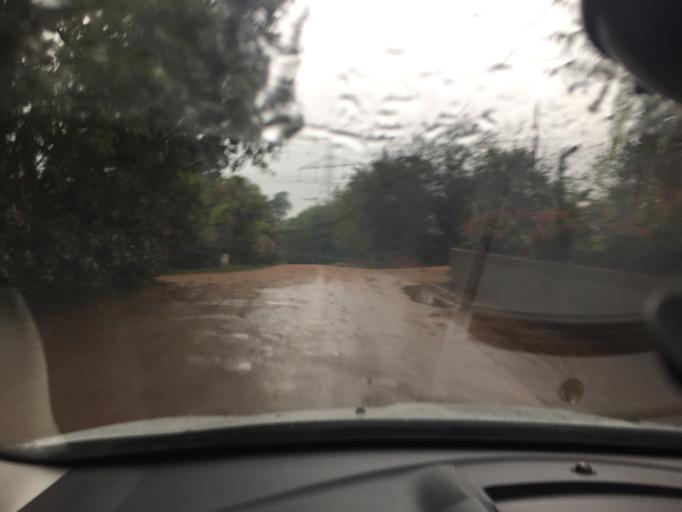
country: BR
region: Sao Paulo
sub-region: Jarinu
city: Jarinu
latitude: -23.1414
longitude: -46.7340
